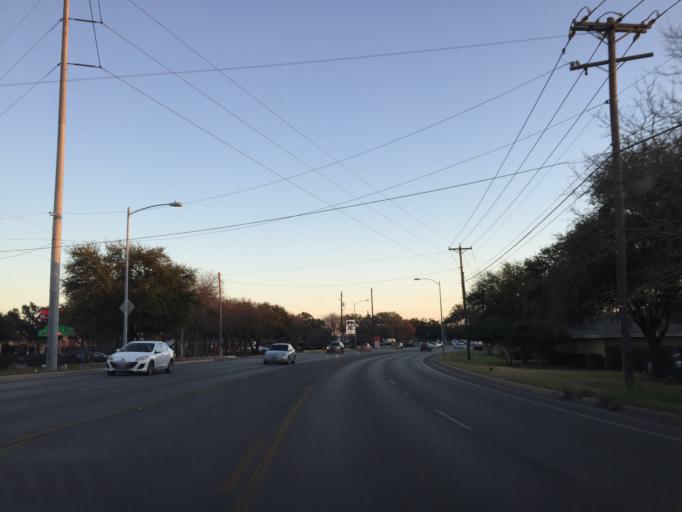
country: US
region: Texas
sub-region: Williamson County
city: Jollyville
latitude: 30.4154
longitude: -97.7482
